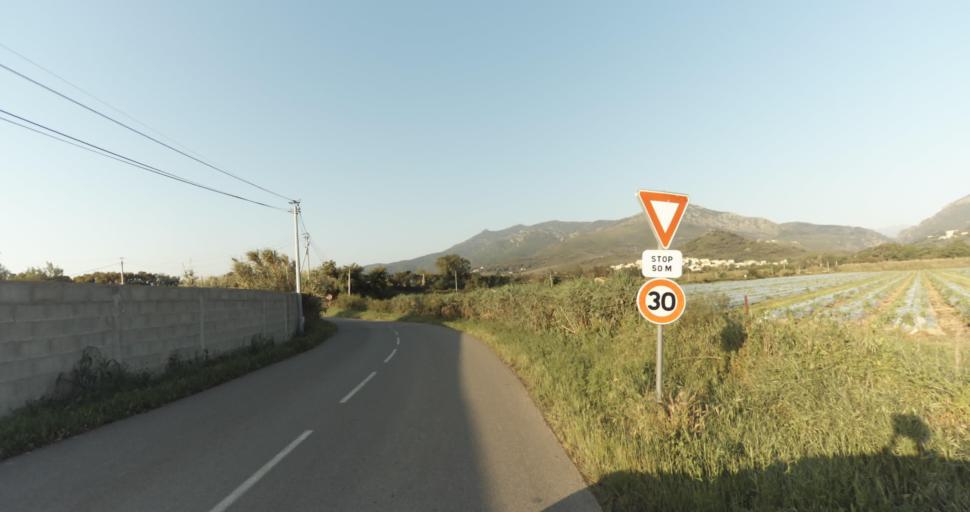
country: FR
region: Corsica
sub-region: Departement de la Haute-Corse
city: Biguglia
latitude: 42.6116
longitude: 9.4425
